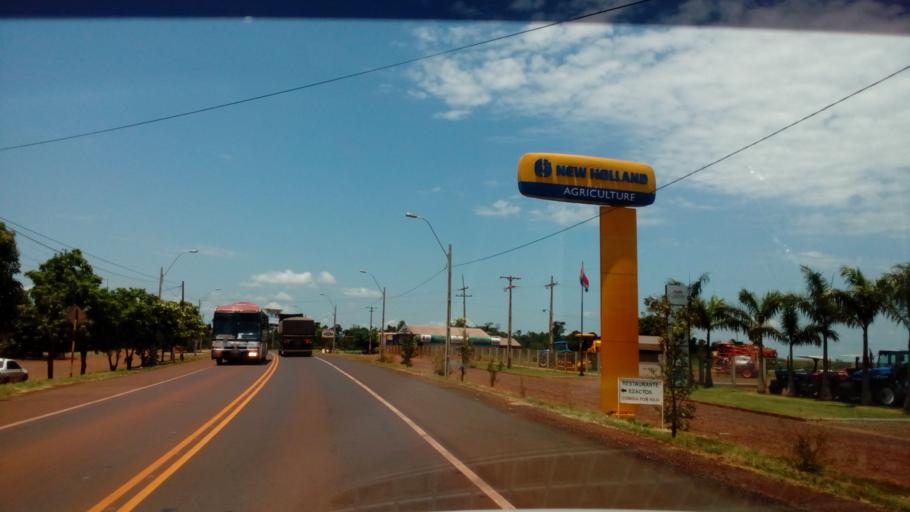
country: PY
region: Alto Parana
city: Santa Rita
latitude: -25.8219
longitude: -55.1136
